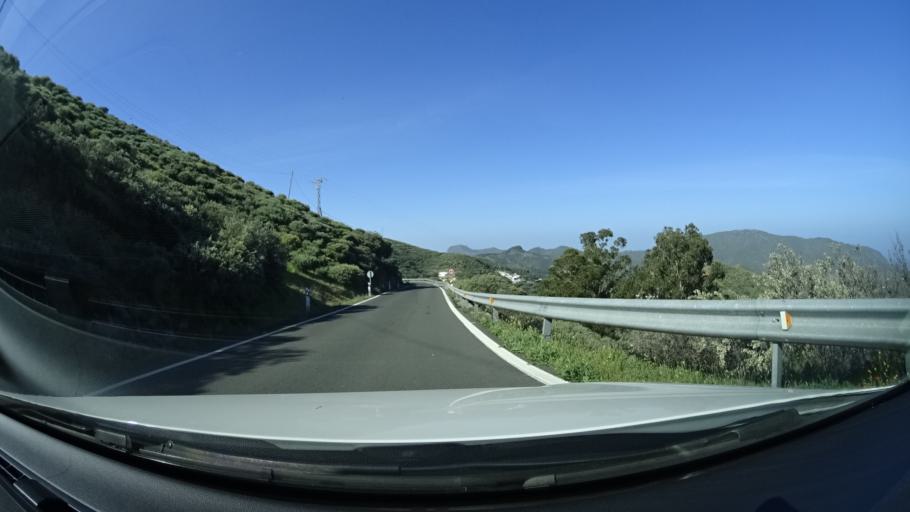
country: ES
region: Canary Islands
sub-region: Provincia de Las Palmas
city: Artenara
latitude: 28.0261
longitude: -15.6332
